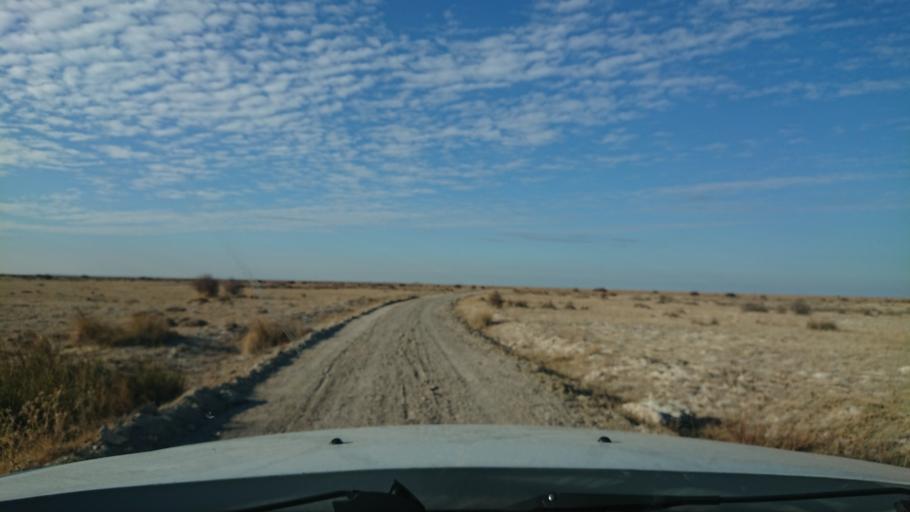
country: TR
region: Aksaray
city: Eskil
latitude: 38.5466
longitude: 33.3192
